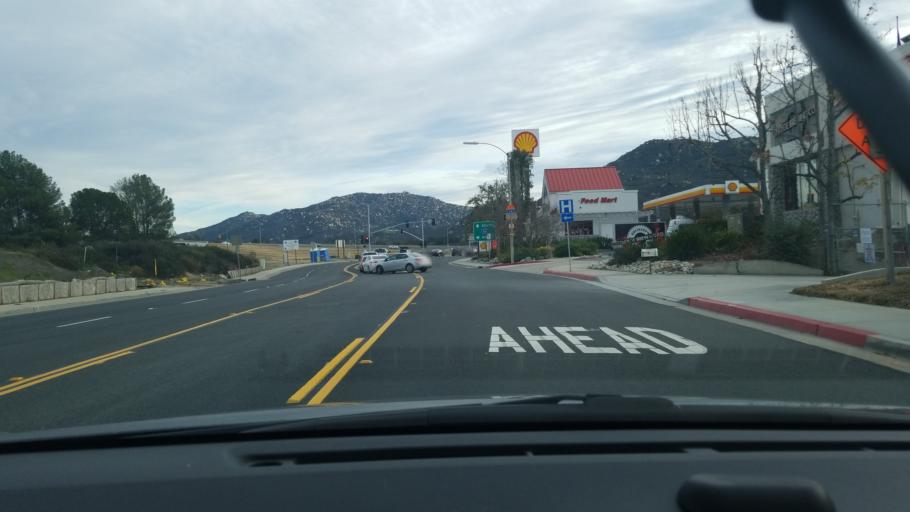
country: US
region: California
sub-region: Riverside County
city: Temecula
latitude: 33.4828
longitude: -117.1433
